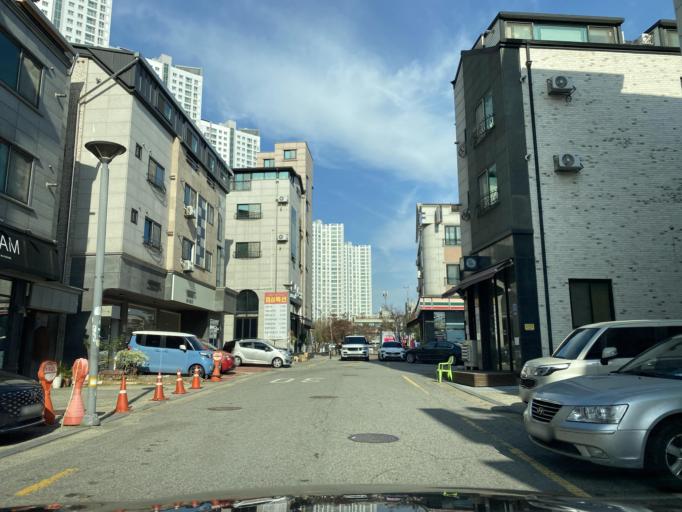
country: KR
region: Chungcheongnam-do
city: Cheonan
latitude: 36.8009
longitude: 127.1060
